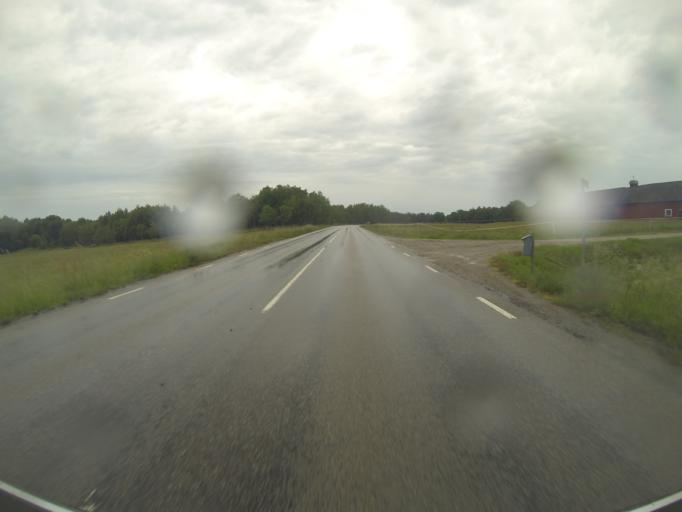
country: SE
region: Blekinge
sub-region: Ronneby Kommun
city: Ronneby
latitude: 56.1727
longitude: 15.3316
